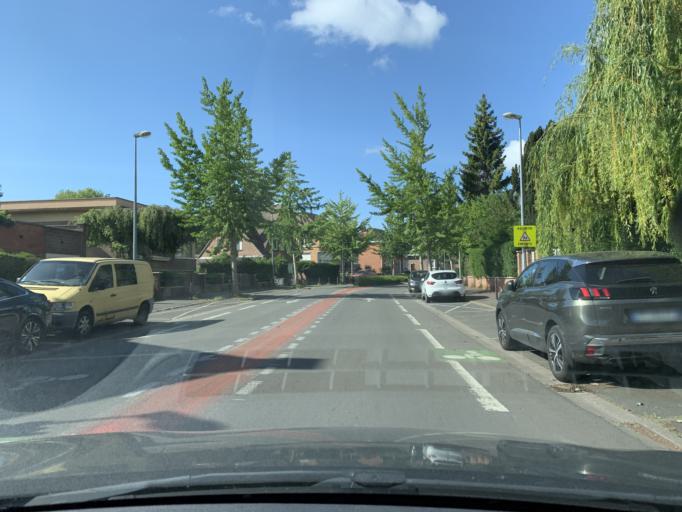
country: FR
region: Nord-Pas-de-Calais
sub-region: Departement du Nord
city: Douai
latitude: 50.3628
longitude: 3.0842
